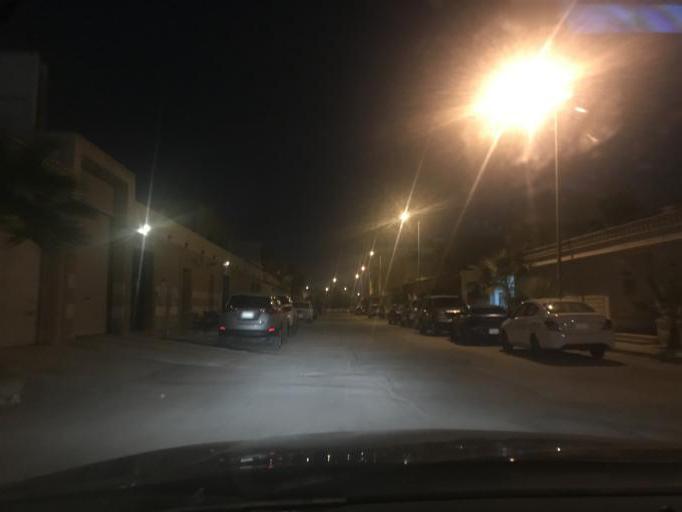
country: SA
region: Ar Riyad
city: Riyadh
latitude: 24.7490
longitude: 46.7523
